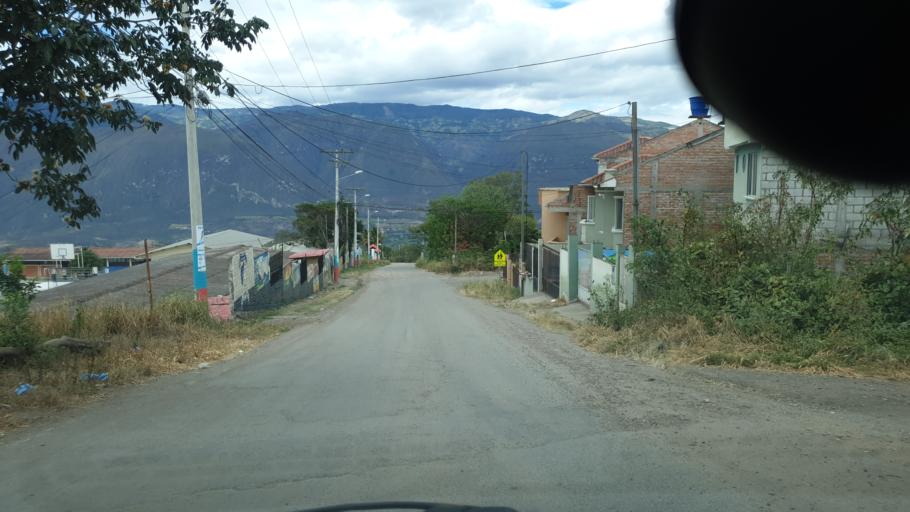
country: EC
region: Azuay
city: Cuenca
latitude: -3.2754
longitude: -79.3122
